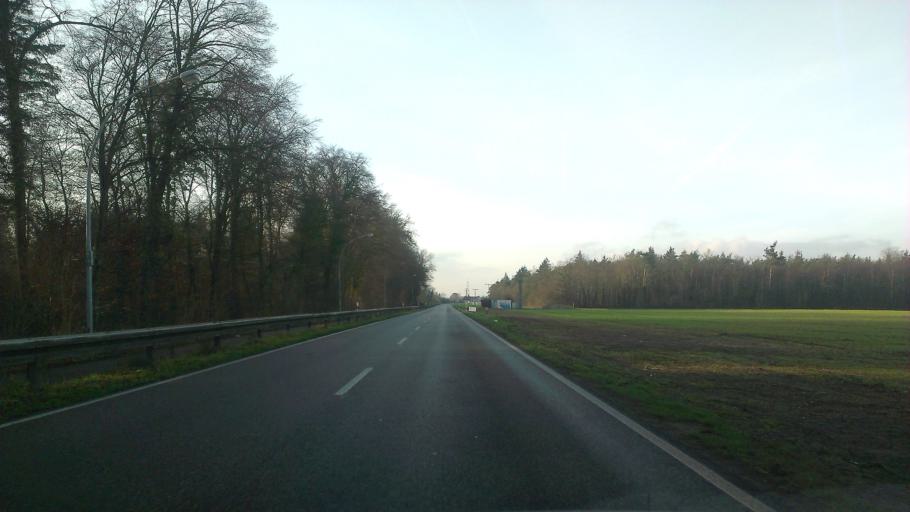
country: DE
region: Baden-Wuerttemberg
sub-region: Karlsruhe Region
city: Waghausel
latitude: 49.2476
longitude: 8.5290
